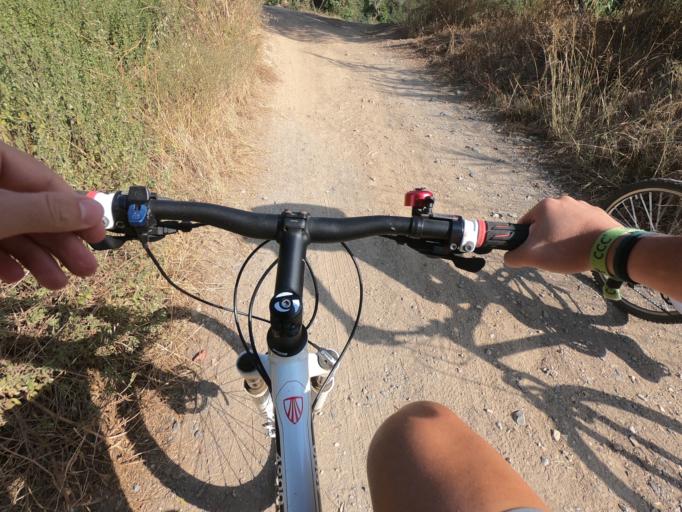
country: ES
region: Catalonia
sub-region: Provincia de Barcelona
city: Sant Just Desvern
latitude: 41.3857
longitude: 2.0659
